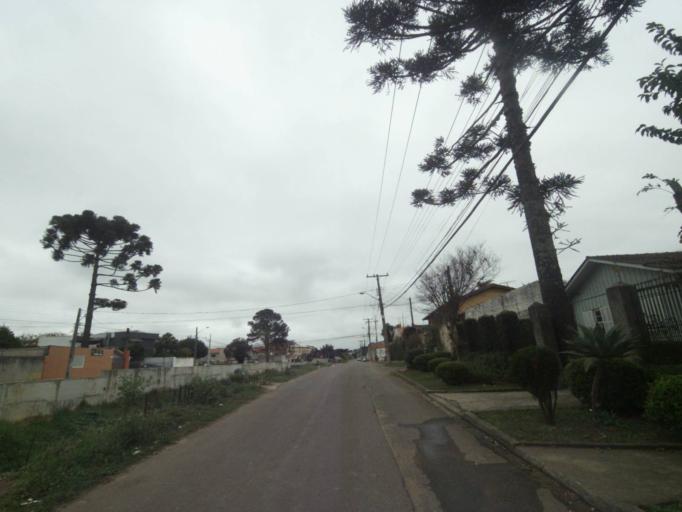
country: BR
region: Parana
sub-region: Curitiba
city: Curitiba
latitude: -25.4646
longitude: -49.2700
